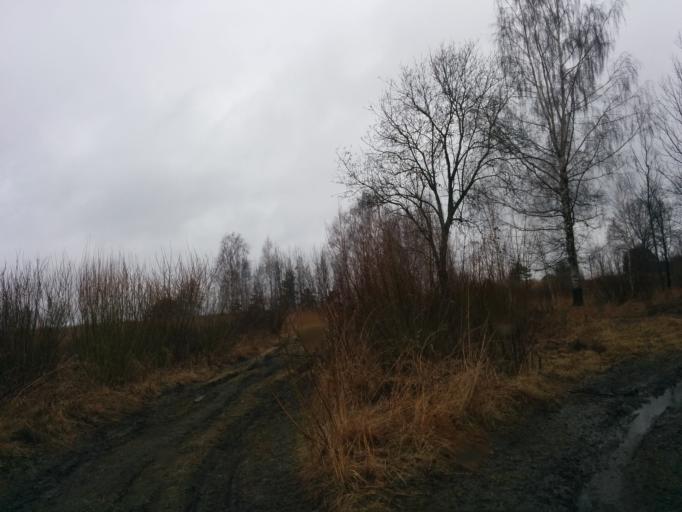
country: LV
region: Jelgava
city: Jelgava
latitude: 56.6821
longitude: 23.7037
